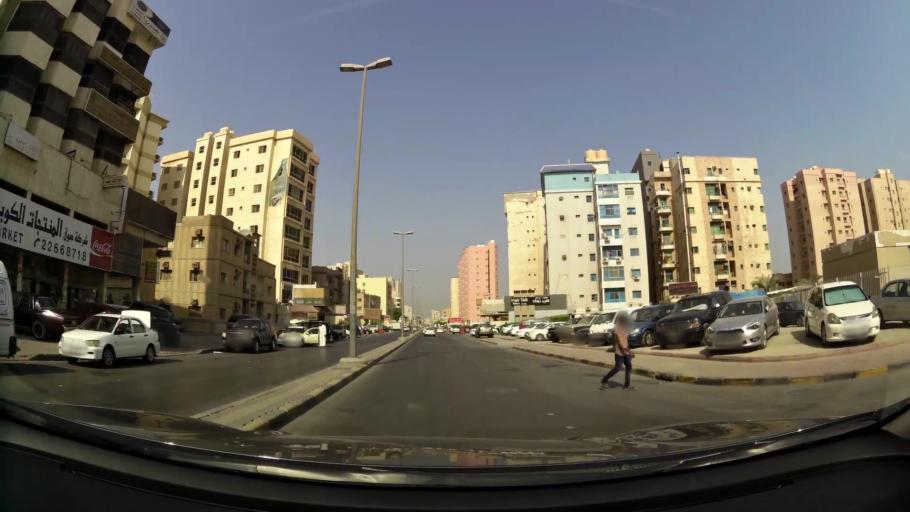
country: KW
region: Muhafazat Hawalli
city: Hawalli
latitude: 29.3363
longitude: 48.0305
